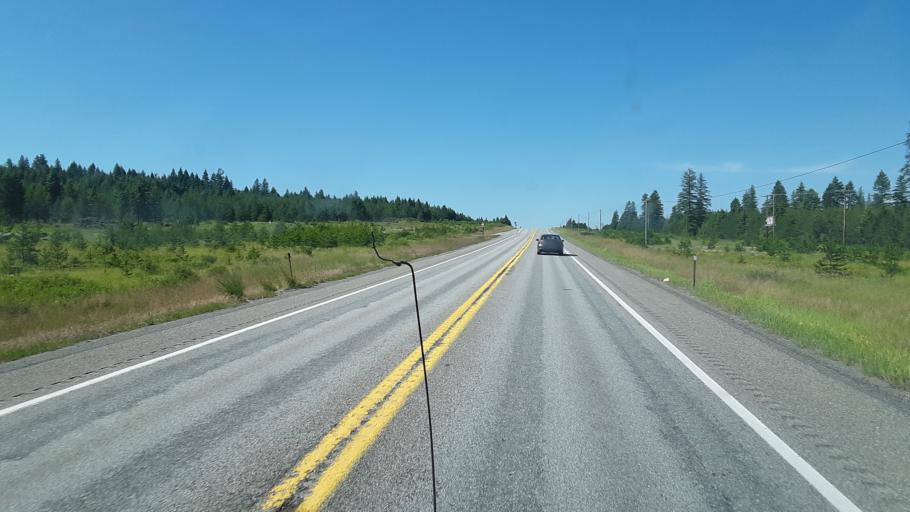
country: US
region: Idaho
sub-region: Kootenai County
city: Spirit Lake
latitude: 48.0109
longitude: -116.6630
